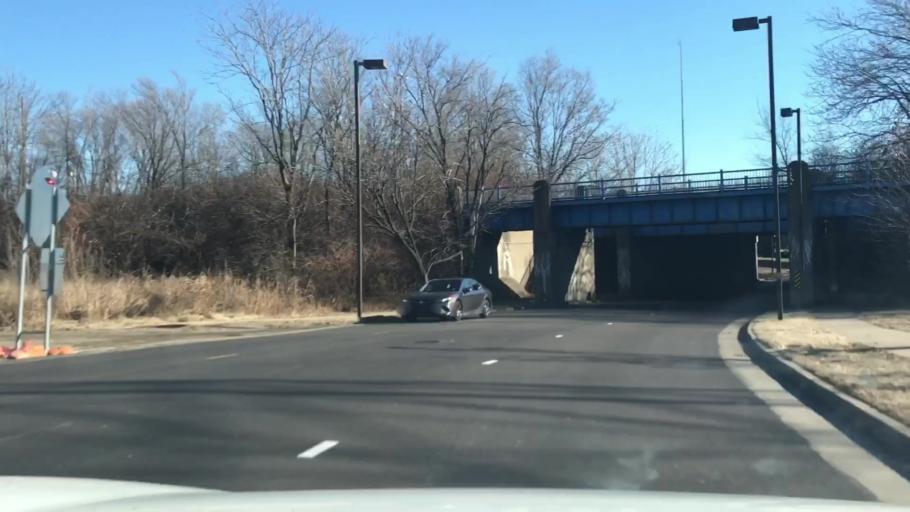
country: US
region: Illinois
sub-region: Saint Clair County
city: East Saint Louis
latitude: 38.6278
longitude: -90.1653
